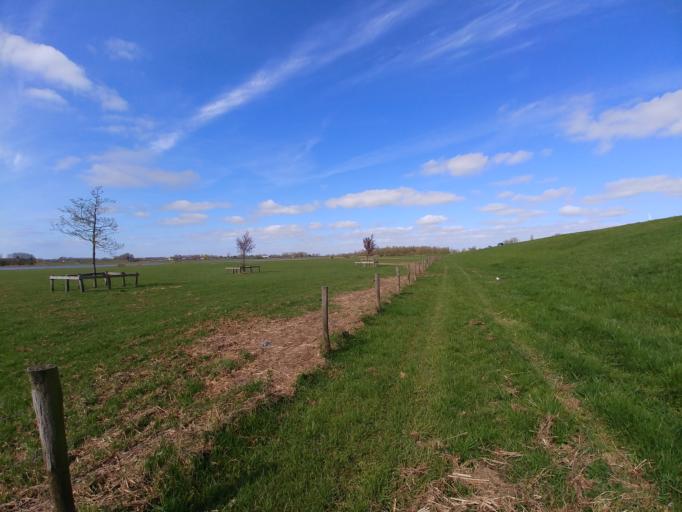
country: NL
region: Overijssel
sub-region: Gemeente Olst-Wijhe
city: Boskamp
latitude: 52.2931
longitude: 6.1172
